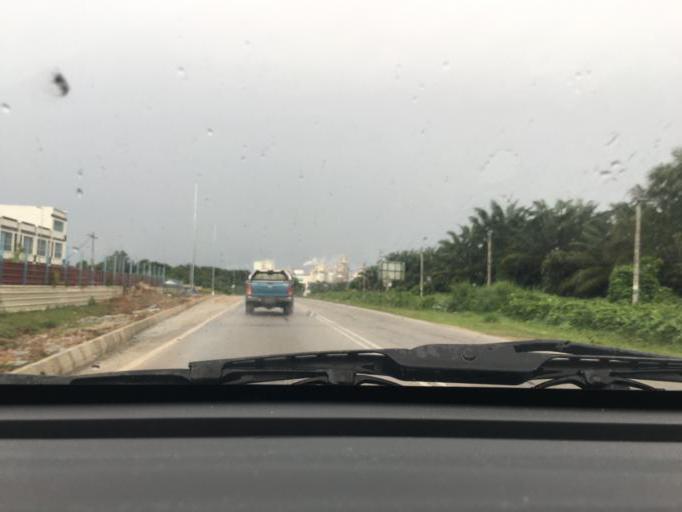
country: MY
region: Kedah
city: Sungai Petani
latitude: 5.6058
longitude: 100.6401
